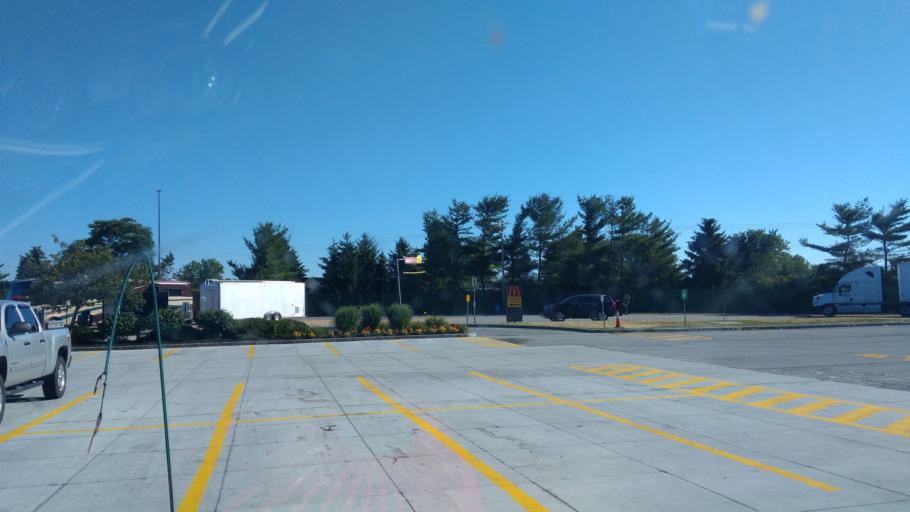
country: US
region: New York
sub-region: Genesee County
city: Bergen
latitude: 43.0308
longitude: -77.9060
